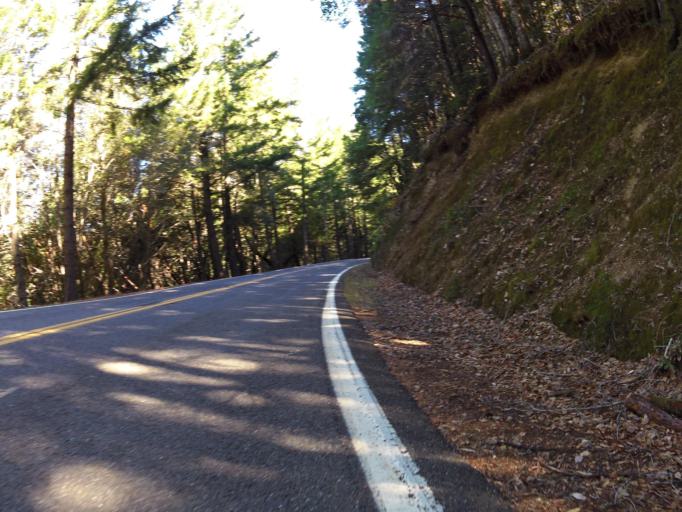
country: US
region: California
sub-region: Humboldt County
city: Redway
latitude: 39.8531
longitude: -123.7445
